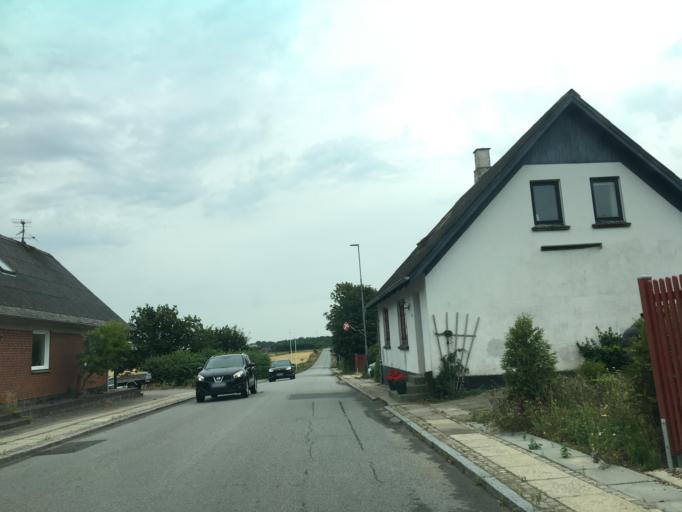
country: DK
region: North Denmark
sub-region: Thisted Kommune
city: Hurup
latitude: 56.8049
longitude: 8.4076
